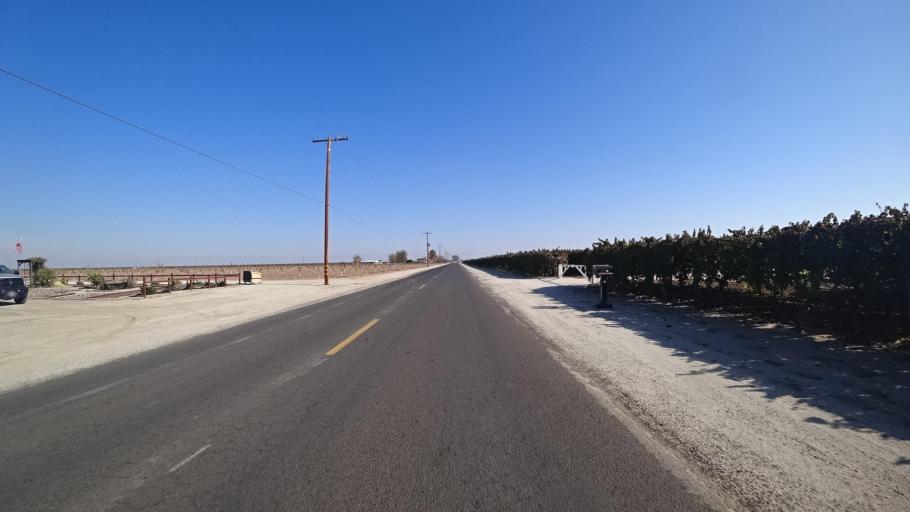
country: US
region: California
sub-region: Kern County
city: McFarland
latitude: 35.6891
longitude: -119.2097
